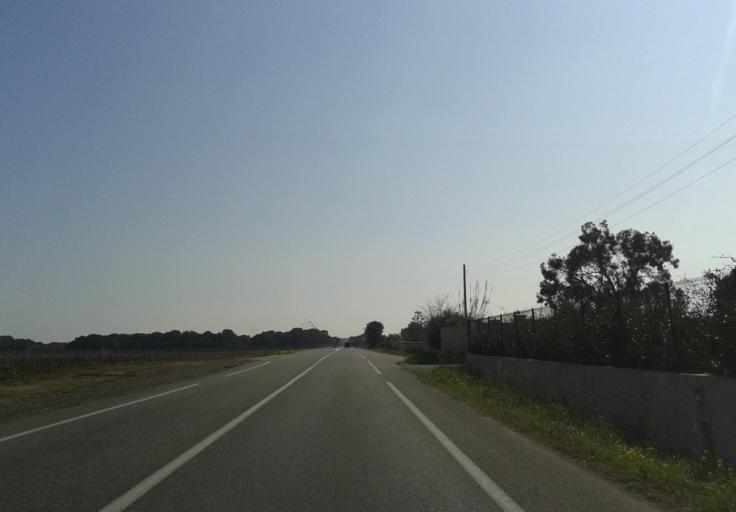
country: FR
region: Corsica
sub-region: Departement de la Haute-Corse
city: Cervione
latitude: 42.2805
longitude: 9.5504
